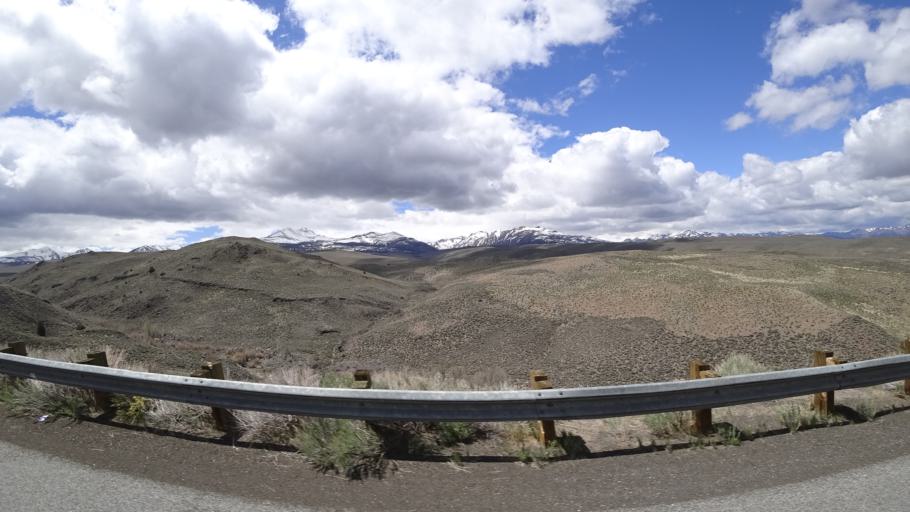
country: US
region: California
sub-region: Mono County
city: Bridgeport
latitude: 38.1364
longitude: -119.1832
